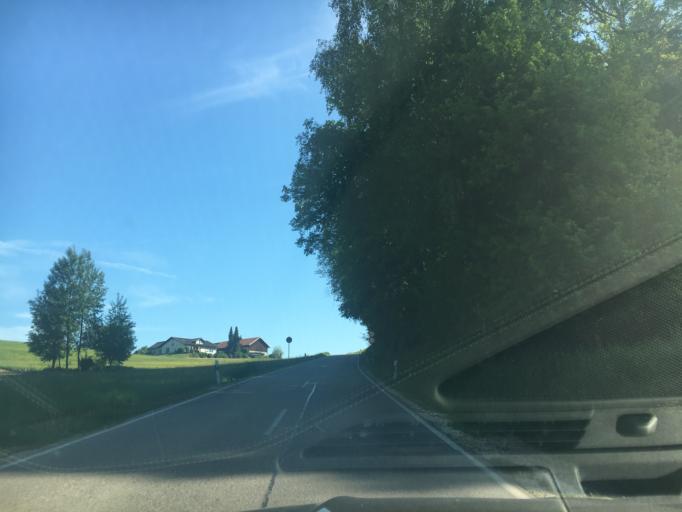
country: DE
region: Bavaria
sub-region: Upper Bavaria
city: Garching an der Alz
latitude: 48.1134
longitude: 12.5961
